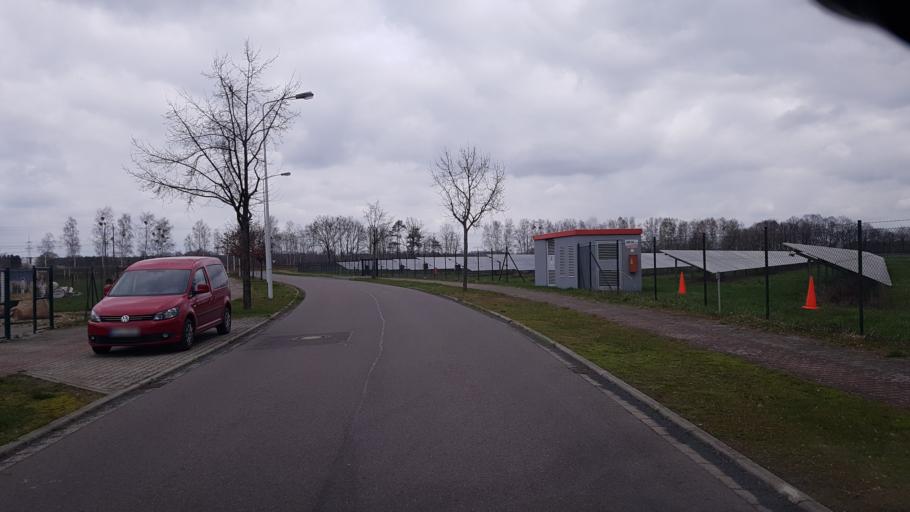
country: DE
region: Brandenburg
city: Ruhland
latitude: 51.4563
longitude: 13.8889
